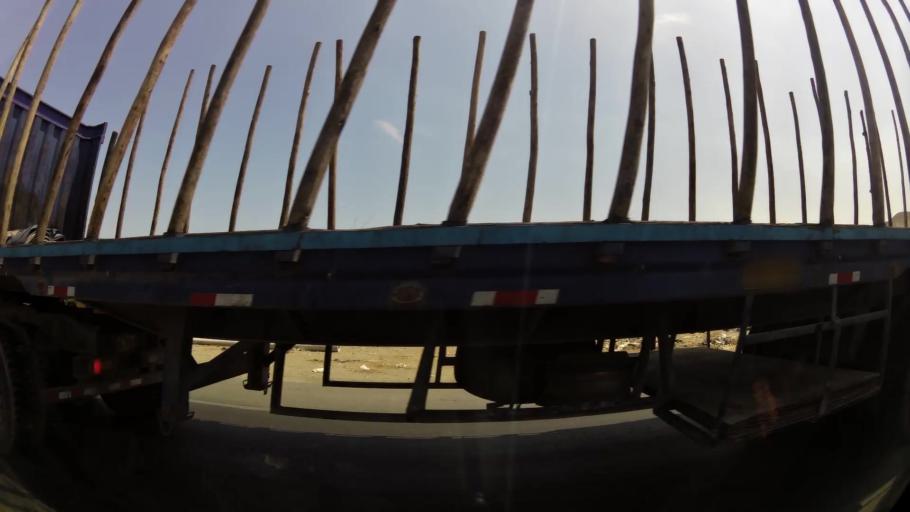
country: PE
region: La Libertad
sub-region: Provincia de Pacasmayo
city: Pacasmayo
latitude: -7.3963
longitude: -79.5576
